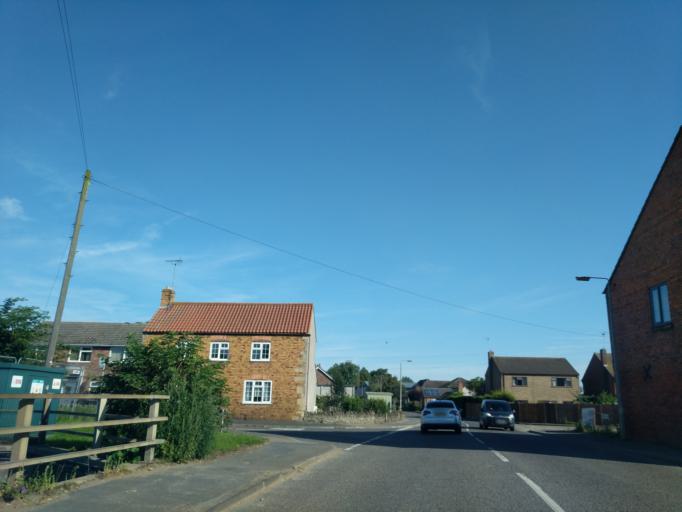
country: GB
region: England
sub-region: Lincolnshire
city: Bourne
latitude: 52.7653
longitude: -0.3625
